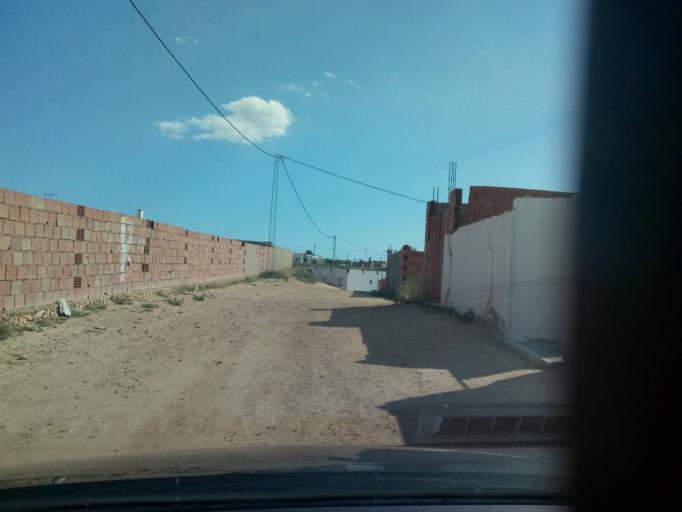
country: TN
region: Safaqis
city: Sfax
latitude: 34.7297
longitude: 10.6046
